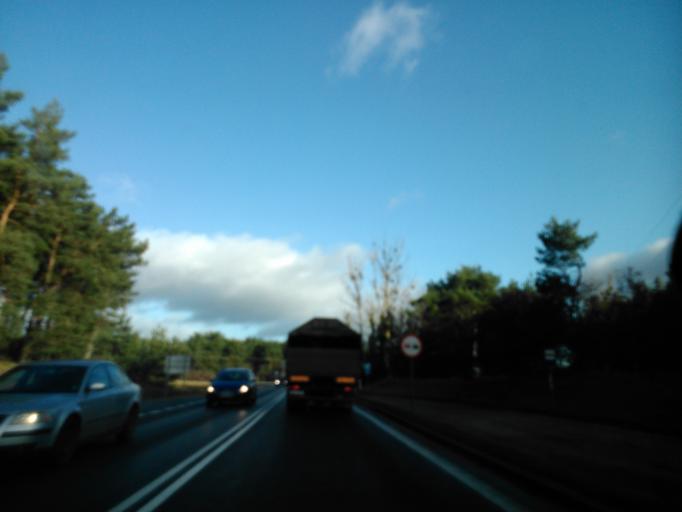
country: PL
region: Kujawsko-Pomorskie
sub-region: Powiat torunski
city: Wielka Nieszawka
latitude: 52.9749
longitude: 18.5431
